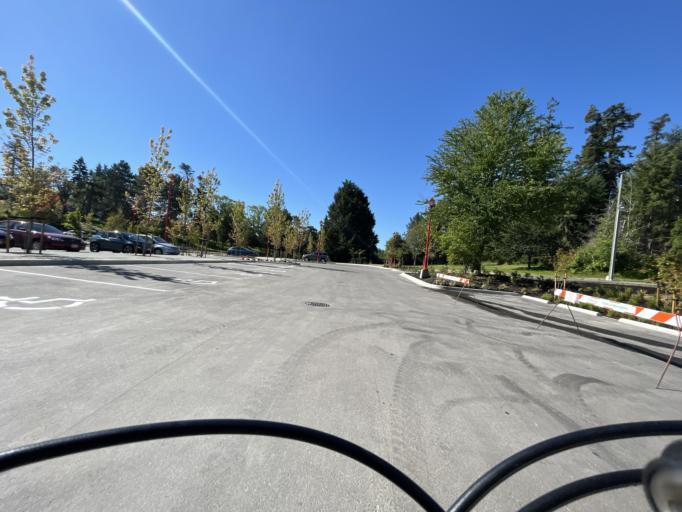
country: CA
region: British Columbia
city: Victoria
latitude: 48.4464
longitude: -123.4053
